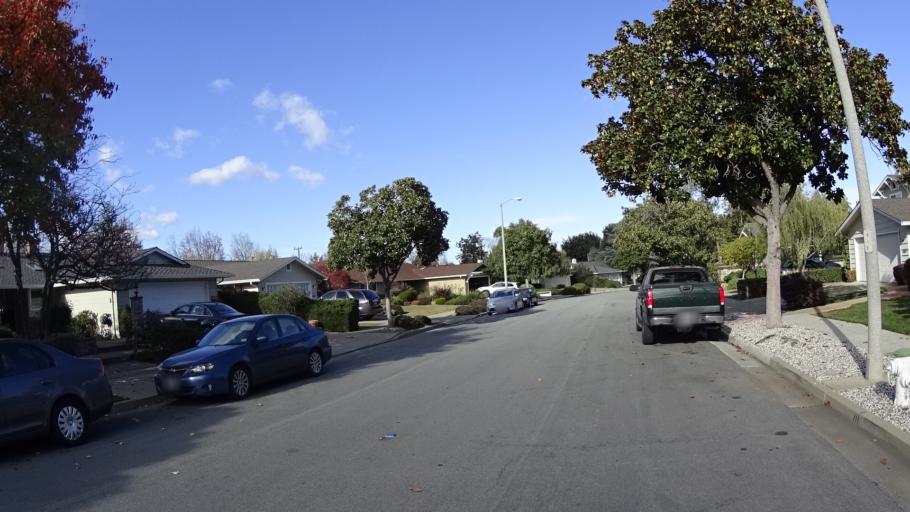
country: US
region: California
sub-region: Santa Clara County
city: Sunnyvale
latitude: 37.3464
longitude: -122.0481
